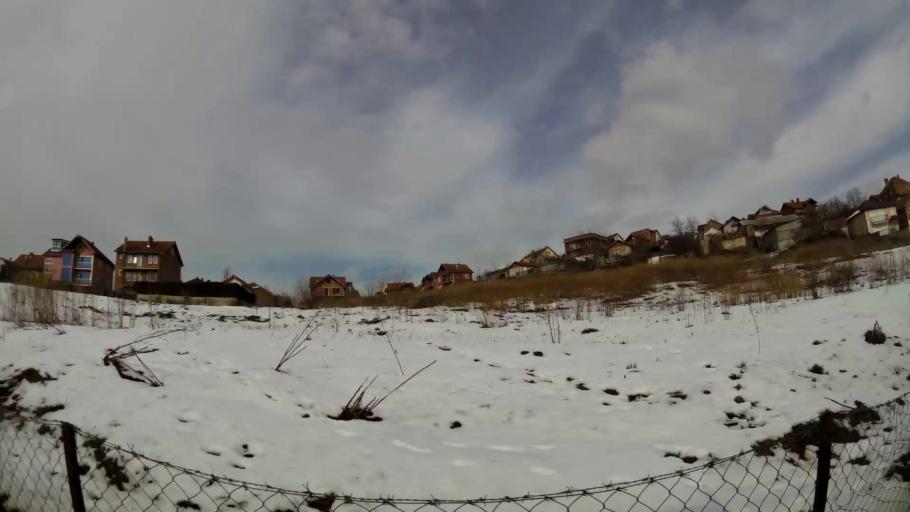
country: XK
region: Pristina
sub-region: Komuna e Prishtines
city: Pristina
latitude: 42.6832
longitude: 21.1686
